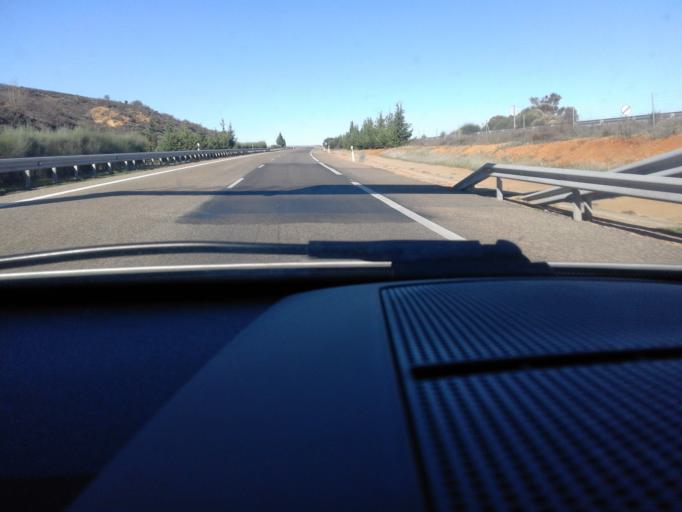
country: ES
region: Castille and Leon
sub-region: Provincia de Leon
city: Onzonilla
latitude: 42.5509
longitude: -5.6246
